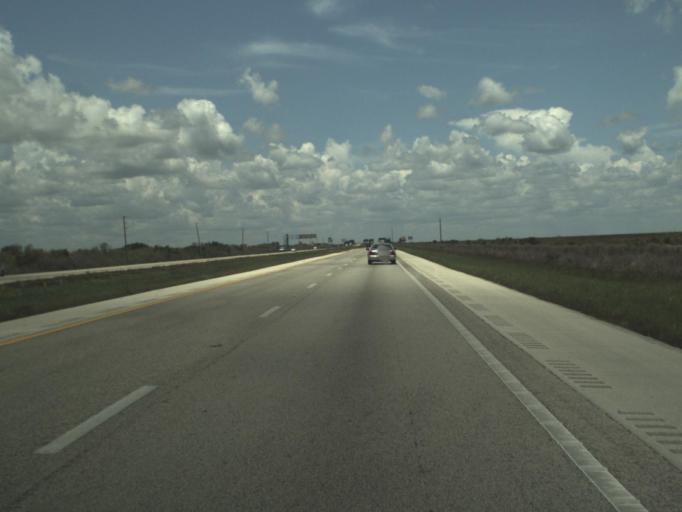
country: US
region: Florida
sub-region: Broward County
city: Weston
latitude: 26.1466
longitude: -80.6521
